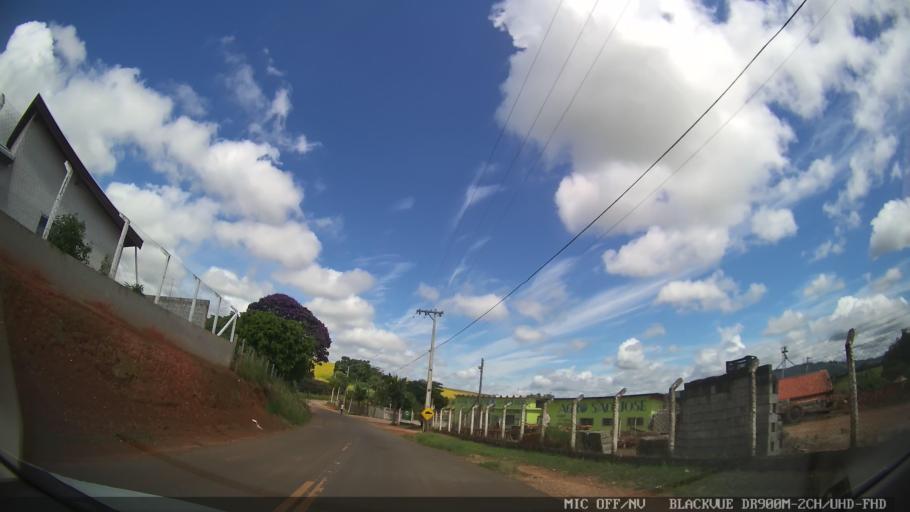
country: BR
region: Sao Paulo
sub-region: Amparo
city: Amparo
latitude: -22.8620
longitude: -46.7062
